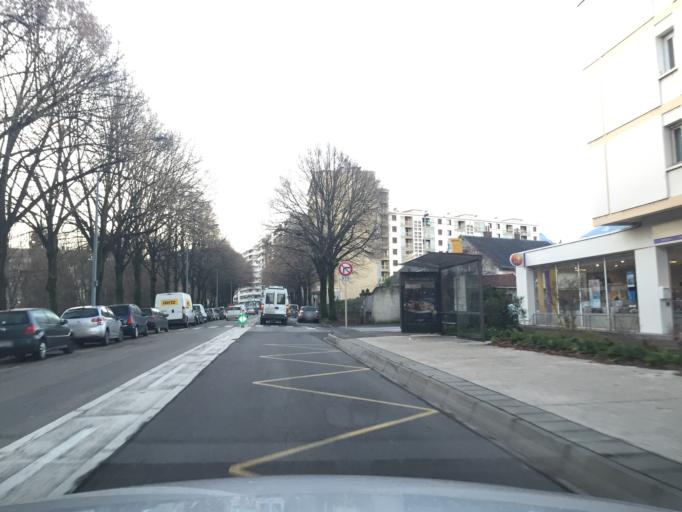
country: FR
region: Rhone-Alpes
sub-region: Departement de la Savoie
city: Chambery
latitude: 45.5758
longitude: 5.9147
